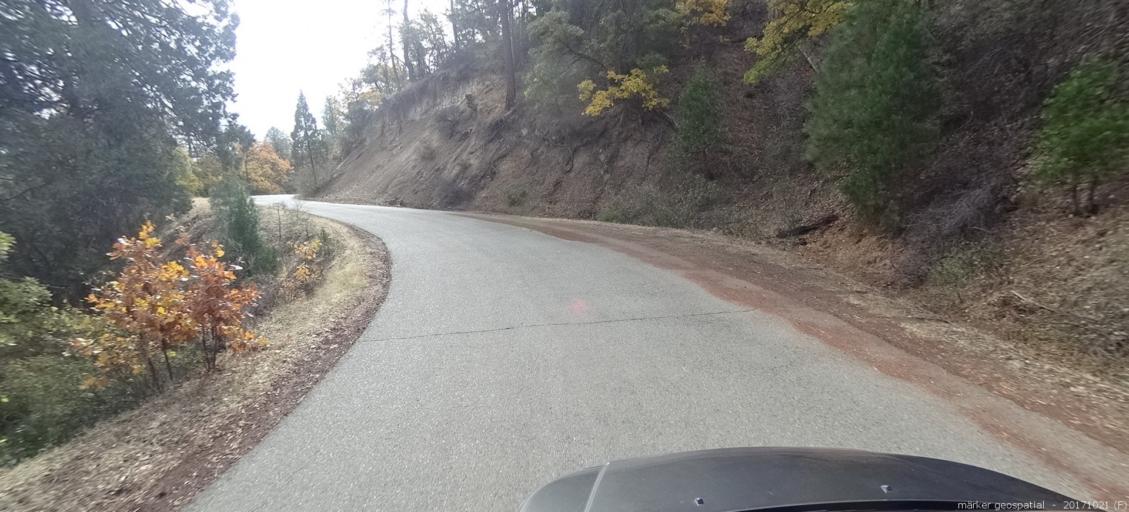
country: US
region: California
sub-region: Shasta County
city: Burney
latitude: 40.9615
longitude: -121.5556
